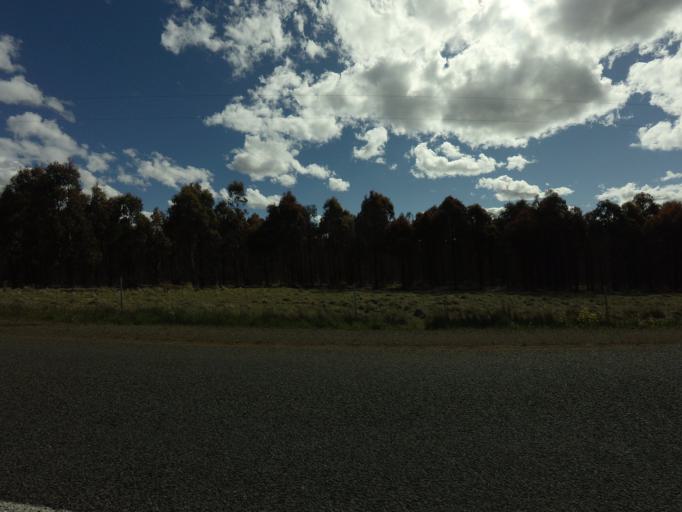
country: AU
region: Tasmania
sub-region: Brighton
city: Bridgewater
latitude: -42.4684
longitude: 147.3206
